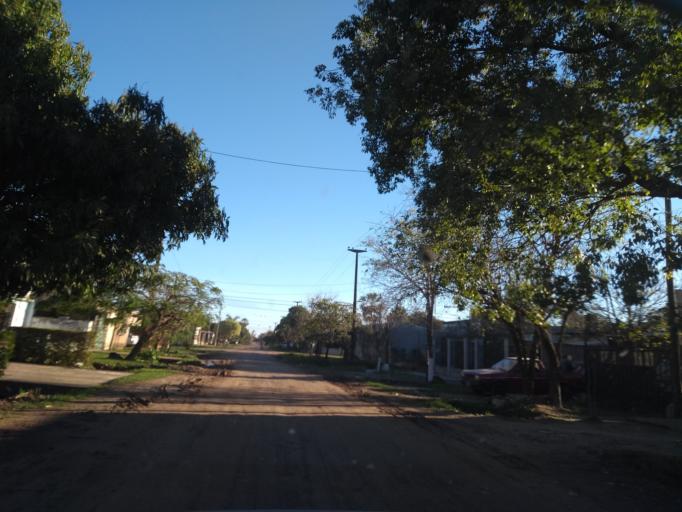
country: AR
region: Chaco
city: Barranqueras
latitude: -27.4887
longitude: -58.9339
